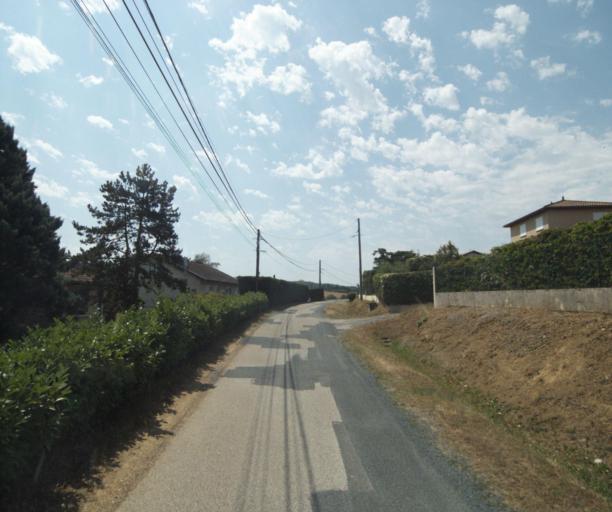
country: FR
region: Rhone-Alpes
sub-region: Departement du Rhone
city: Saint-Germain-Nuelles
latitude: 45.8449
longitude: 4.6315
